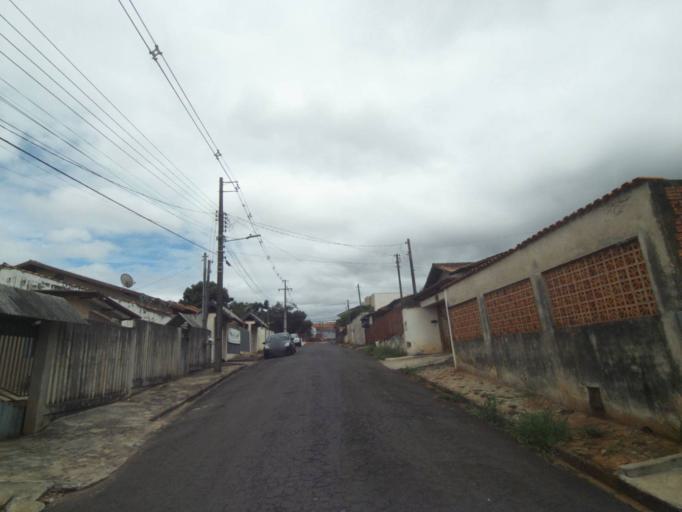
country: BR
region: Parana
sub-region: Telemaco Borba
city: Telemaco Borba
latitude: -24.3323
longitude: -50.6151
